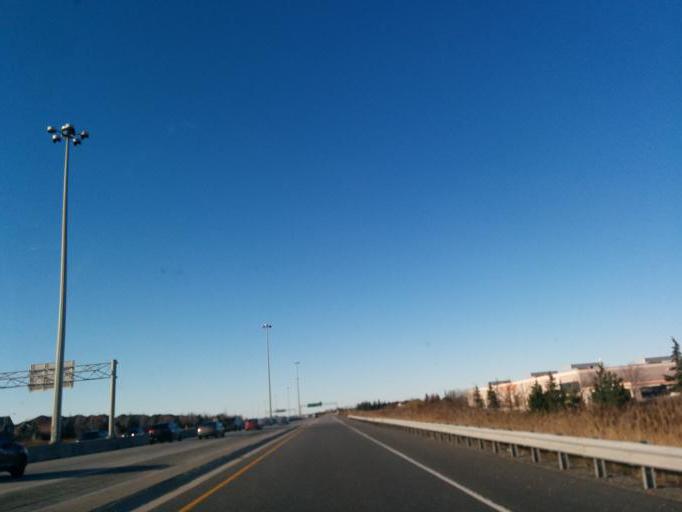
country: CA
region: Ontario
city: Brampton
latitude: 43.7291
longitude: -79.7677
